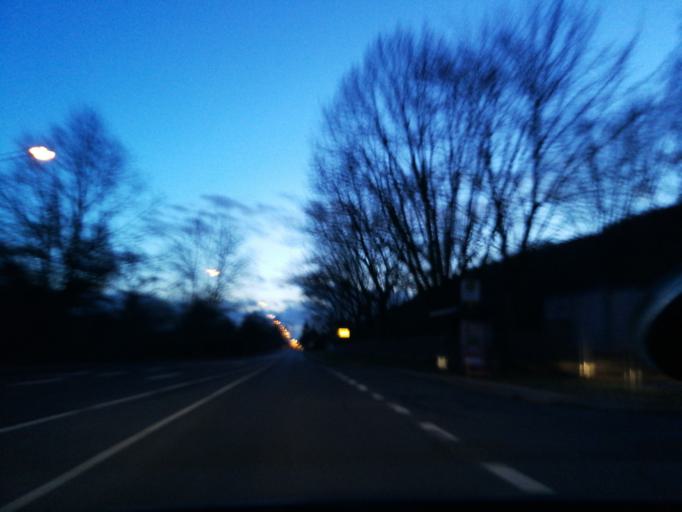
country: DE
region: Rheinland-Pfalz
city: Kenn
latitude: 49.7873
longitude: 6.6752
